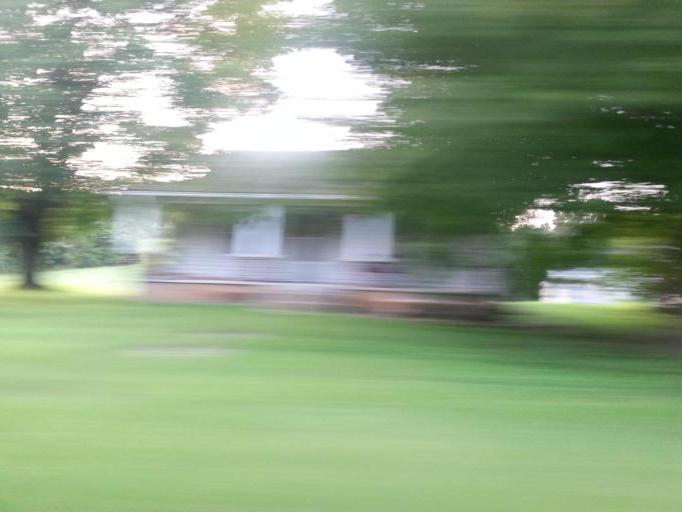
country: US
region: Tennessee
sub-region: Union County
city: Condon
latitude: 36.1932
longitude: -83.7728
